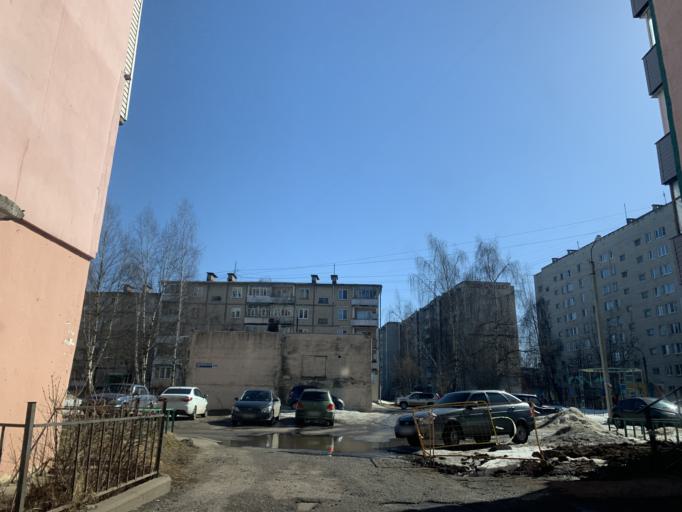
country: RU
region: Jaroslavl
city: Tutayev
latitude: 57.8664
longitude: 39.5100
